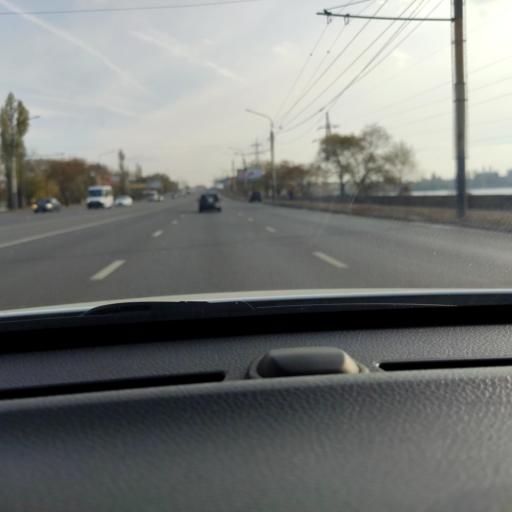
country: RU
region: Voronezj
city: Voronezh
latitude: 51.6357
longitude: 39.2138
